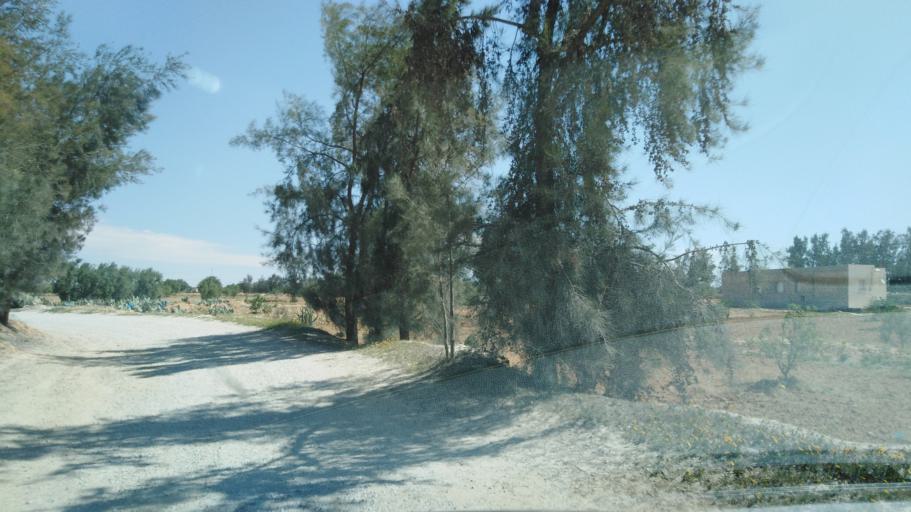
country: TN
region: Safaqis
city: Sfax
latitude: 34.7558
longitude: 10.5299
